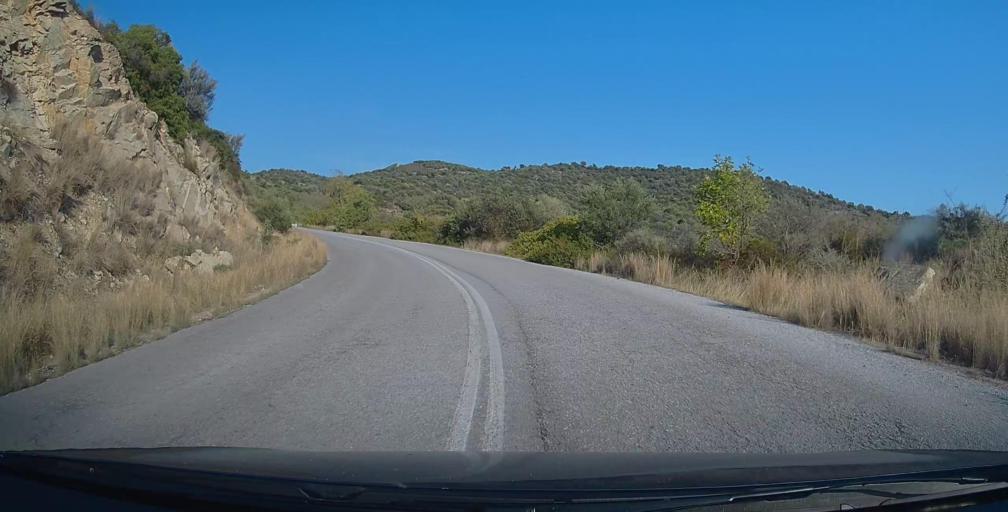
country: GR
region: Central Macedonia
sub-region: Nomos Chalkidikis
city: Sykia
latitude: 40.0140
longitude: 23.8715
